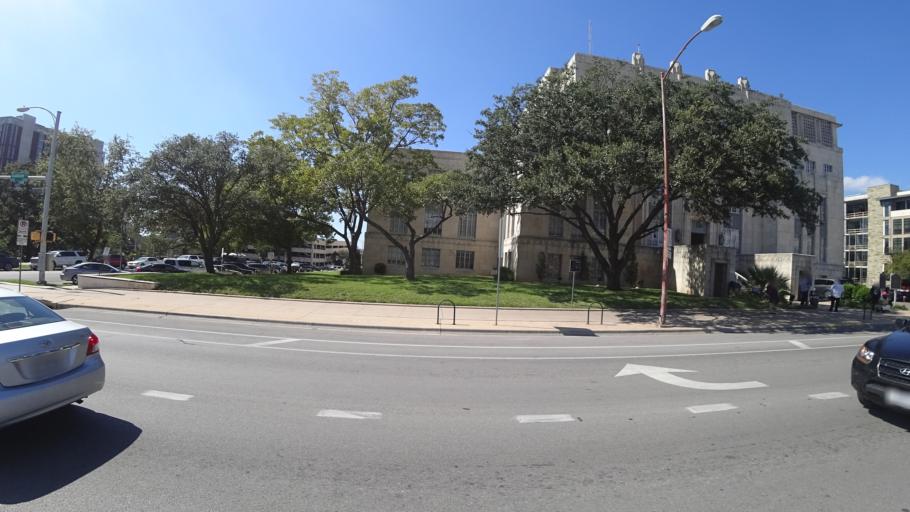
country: US
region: Texas
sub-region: Travis County
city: Austin
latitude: 30.2731
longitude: -97.7448
